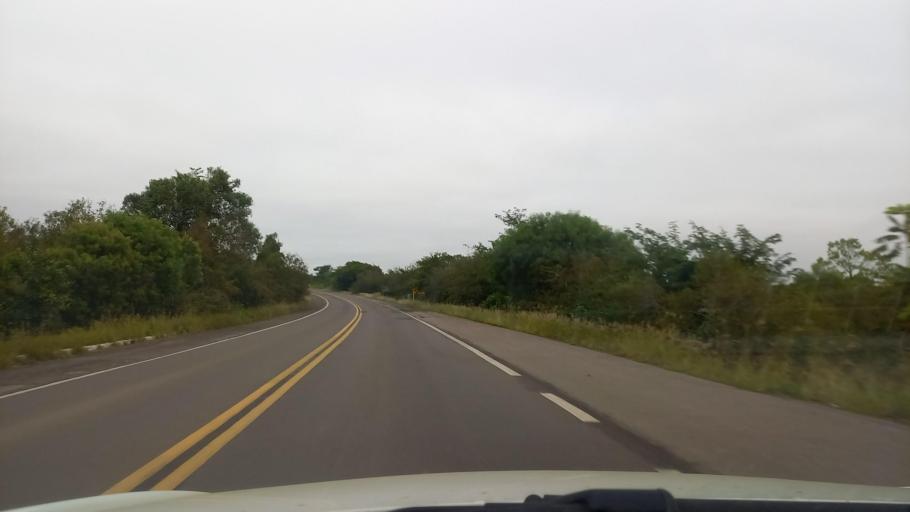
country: BR
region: Rio Grande do Sul
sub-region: Sao Pedro Do Sul
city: Sao Pedro do Sul
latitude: -29.7853
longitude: -54.1140
